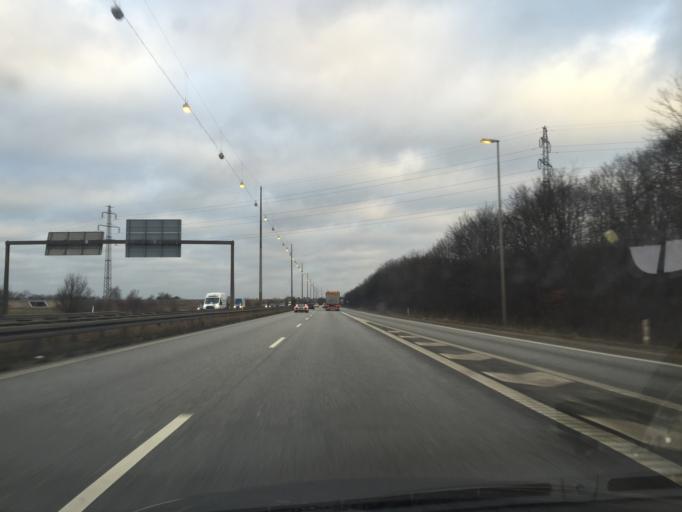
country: DK
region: Capital Region
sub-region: Ishoj Kommune
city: Ishoj
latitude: 55.6250
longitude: 12.3288
